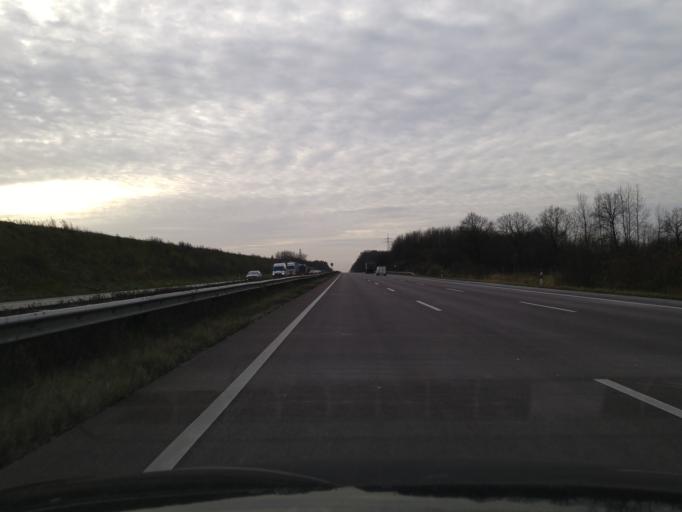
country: DE
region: Schleswig-Holstein
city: Hoisdorf
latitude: 53.6730
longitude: 10.3078
